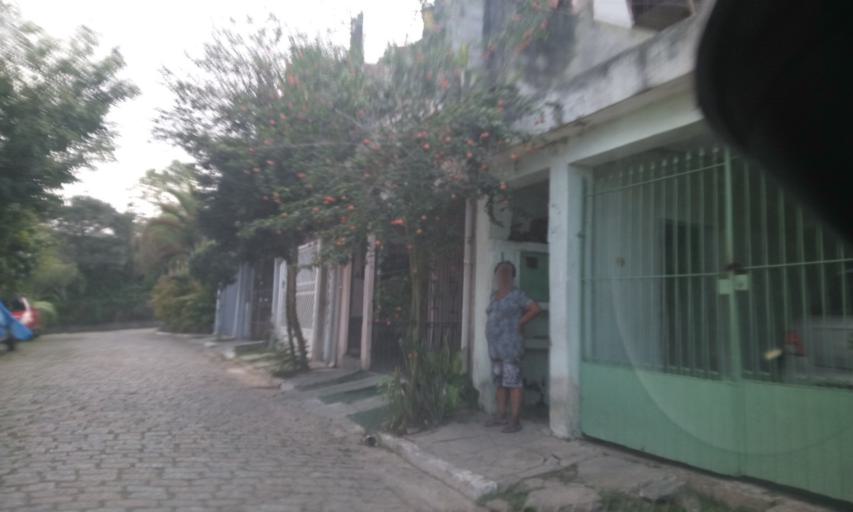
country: BR
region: Sao Paulo
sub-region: Sao Bernardo Do Campo
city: Sao Bernardo do Campo
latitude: -23.7816
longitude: -46.5290
